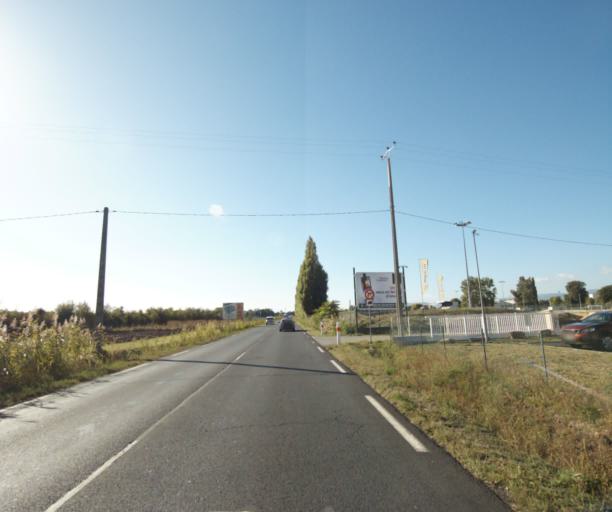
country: FR
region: Auvergne
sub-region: Departement du Puy-de-Dome
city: Gerzat
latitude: 45.8342
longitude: 3.1584
